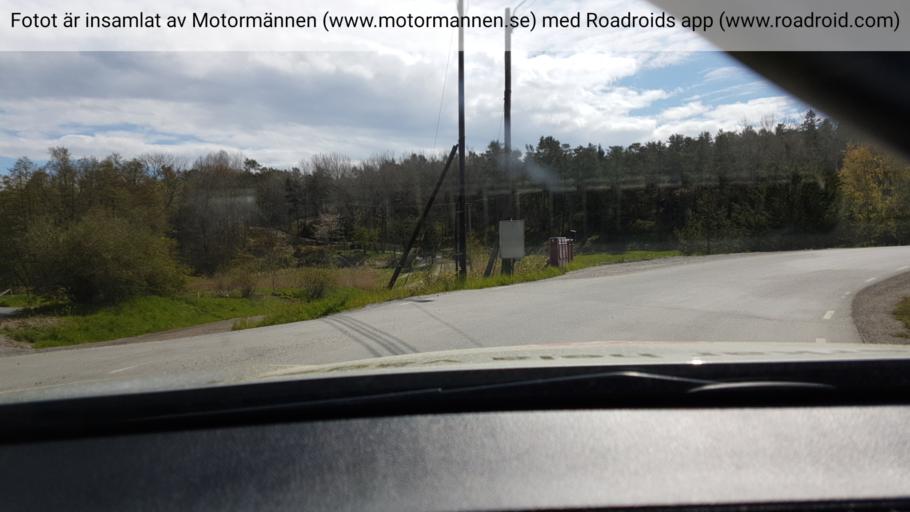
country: SE
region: Stockholm
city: Dalaro
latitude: 59.1658
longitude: 18.4522
